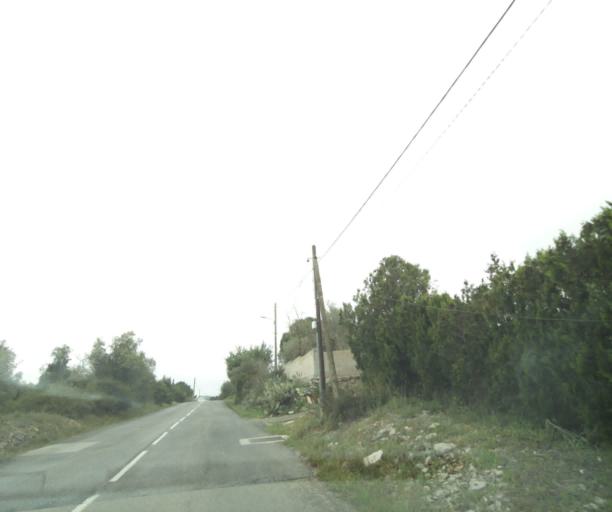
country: FR
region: Languedoc-Roussillon
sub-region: Departement de l'Herault
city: Pignan
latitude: 43.5897
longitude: 3.7533
